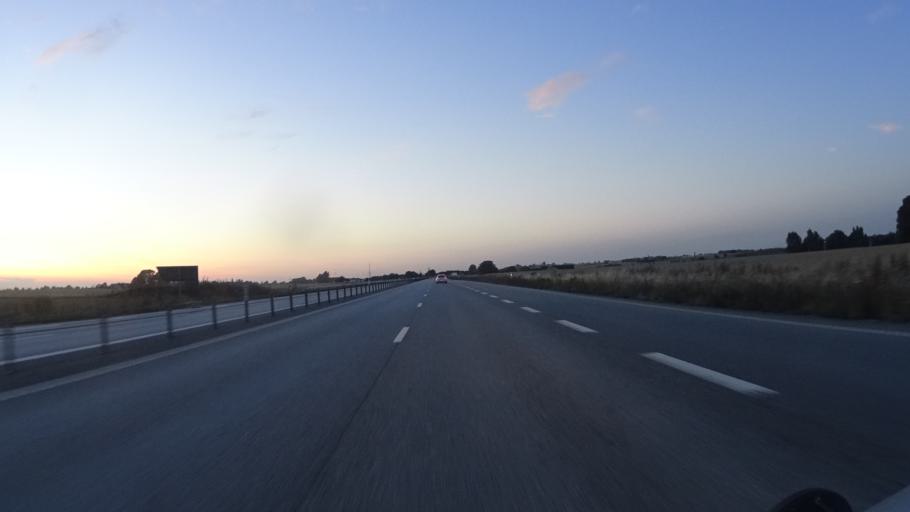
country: SE
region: Skane
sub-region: Trelleborgs Kommun
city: Skare
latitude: 55.4121
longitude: 13.0638
